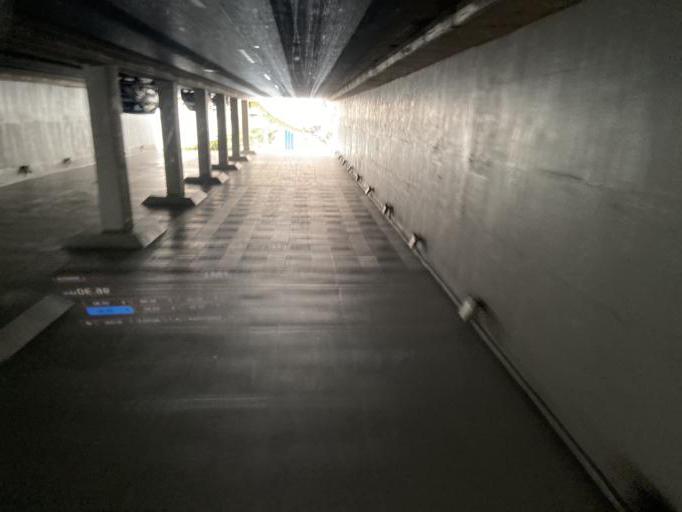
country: SG
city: Singapore
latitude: 1.1402
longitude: 104.0232
